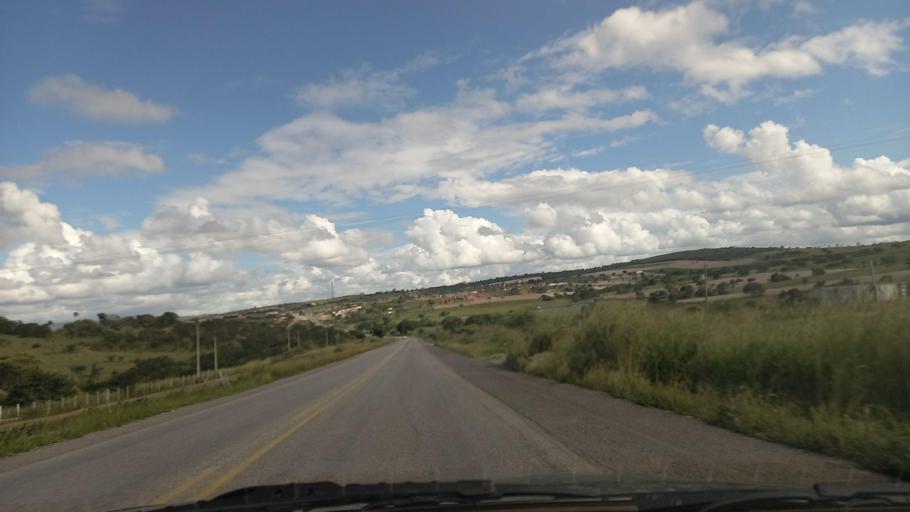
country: BR
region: Pernambuco
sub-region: Lajedo
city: Lajedo
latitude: -8.7426
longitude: -36.4310
